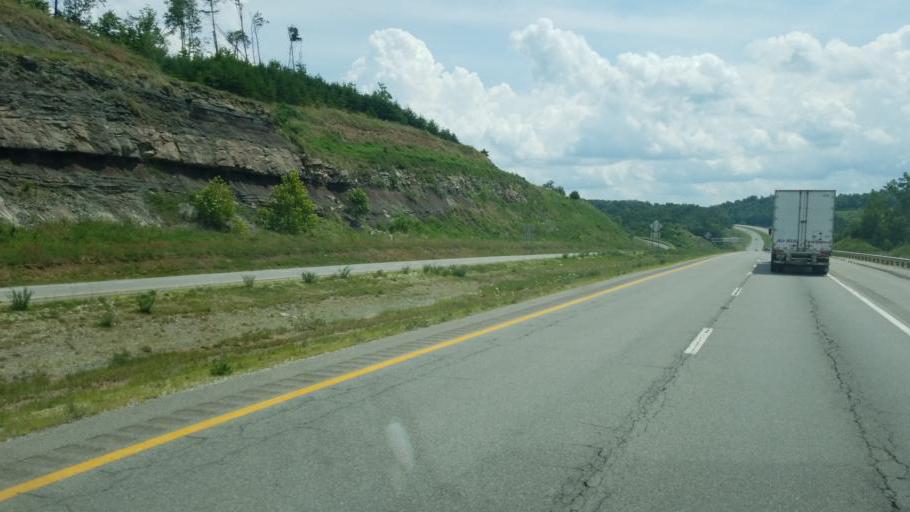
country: US
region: West Virginia
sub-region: Putnam County
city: Buffalo
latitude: 38.5741
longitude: -82.0155
